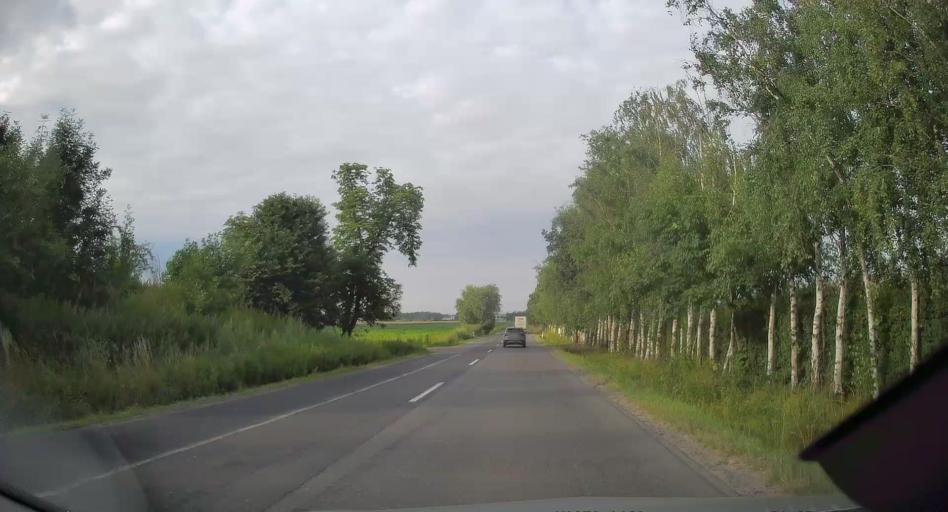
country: PL
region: Lower Silesian Voivodeship
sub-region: Powiat wroclawski
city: Tyniec Maly
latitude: 51.0305
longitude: 16.8883
